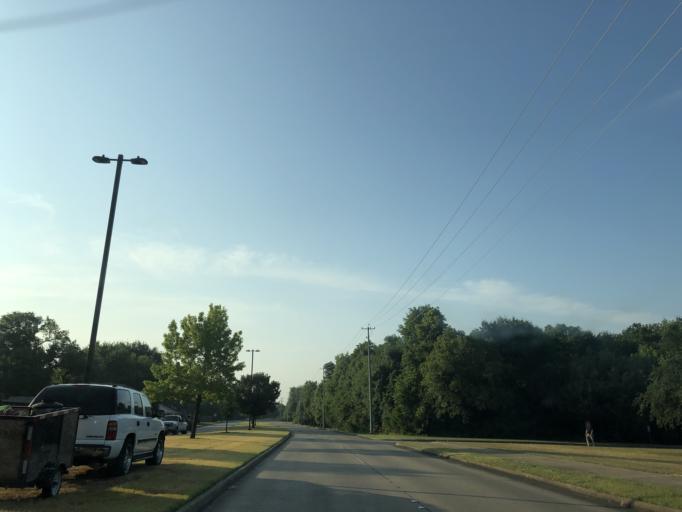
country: US
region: Texas
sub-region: Dallas County
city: Garland
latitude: 32.8659
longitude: -96.6258
